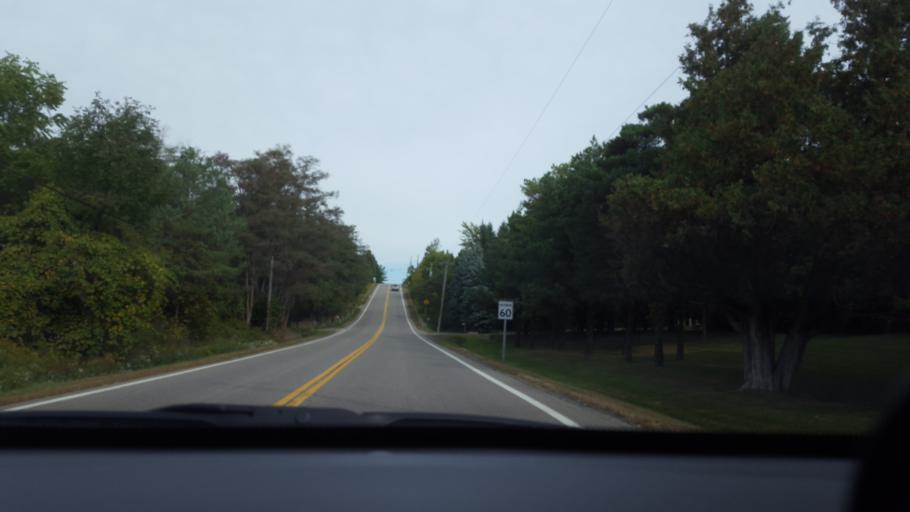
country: CA
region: Ontario
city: Newmarket
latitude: 43.9806
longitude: -79.5425
